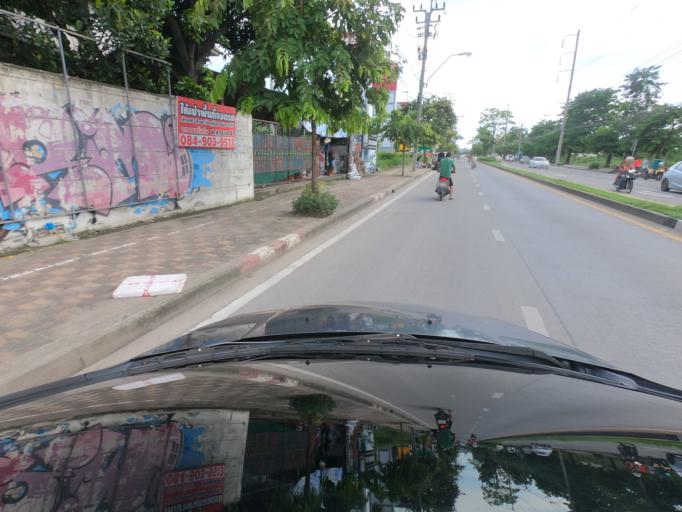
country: TH
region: Bangkok
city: Bang Na
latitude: 13.6585
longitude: 100.6237
